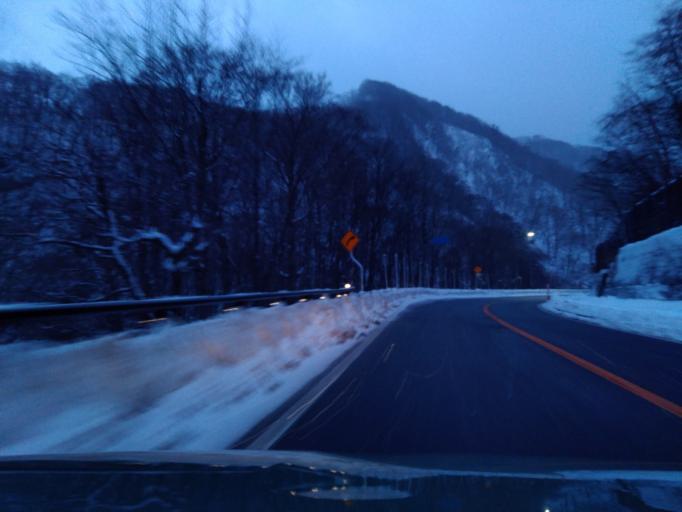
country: JP
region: Iwate
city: Shizukuishi
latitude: 39.7215
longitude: 140.8349
